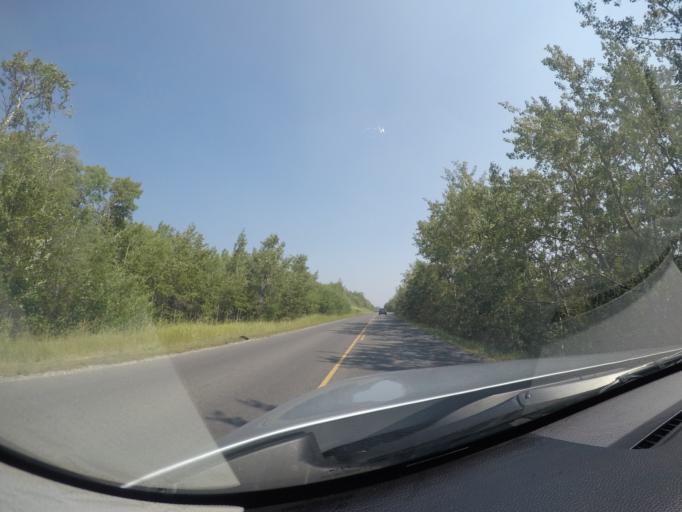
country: US
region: Montana
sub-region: Glacier County
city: North Browning
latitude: 48.7375
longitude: -113.4588
